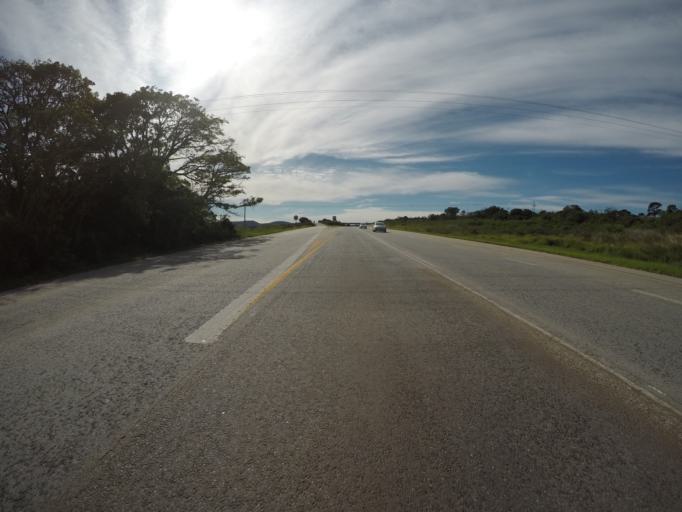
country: ZA
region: Eastern Cape
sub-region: Cacadu District Municipality
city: Jeffrey's Bay
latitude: -33.8994
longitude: 25.1170
